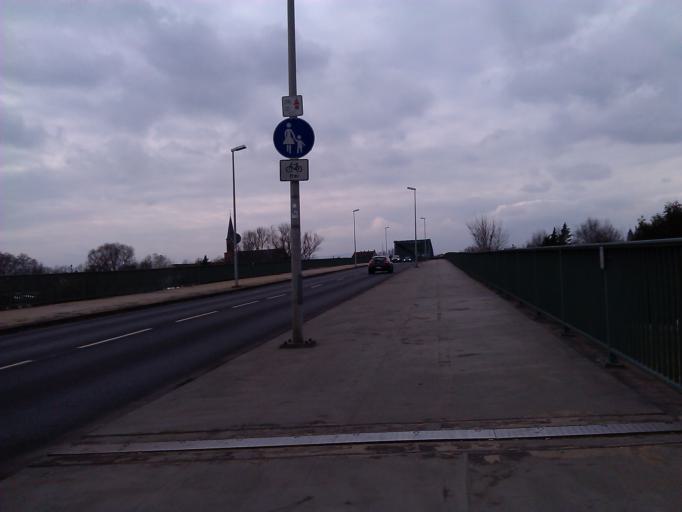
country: DE
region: Rheinland-Pfalz
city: Mainz
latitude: 49.9979
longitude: 8.3122
